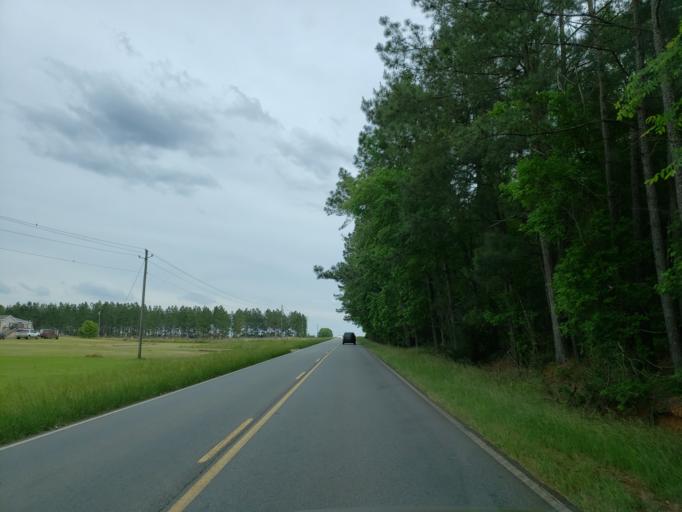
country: US
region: Georgia
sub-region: Macon County
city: Montezuma
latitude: 32.2330
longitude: -83.9510
